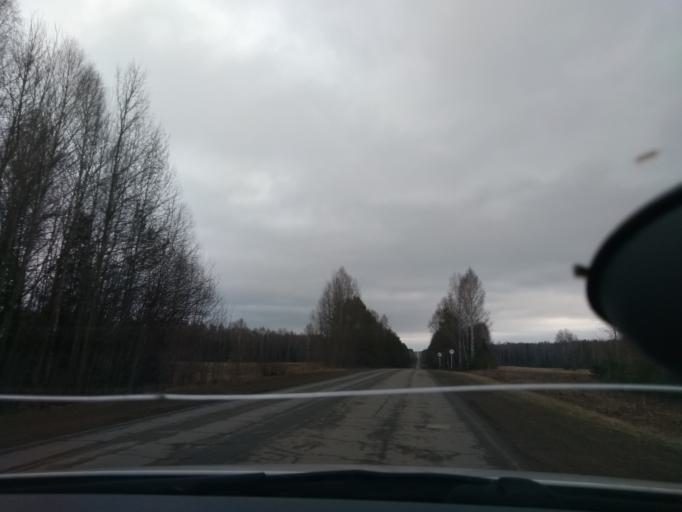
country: RU
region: Perm
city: Kungur
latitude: 57.3656
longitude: 56.8250
